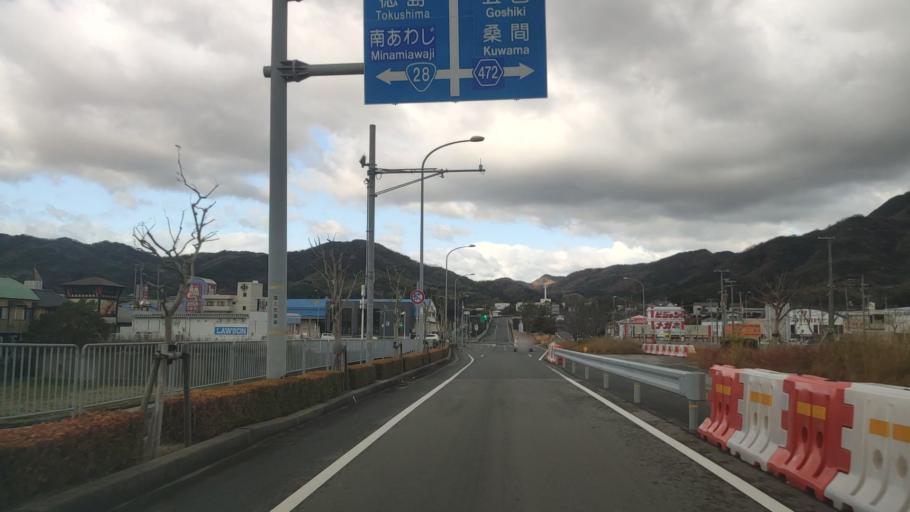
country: JP
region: Hyogo
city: Sumoto
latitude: 34.3374
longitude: 134.8482
